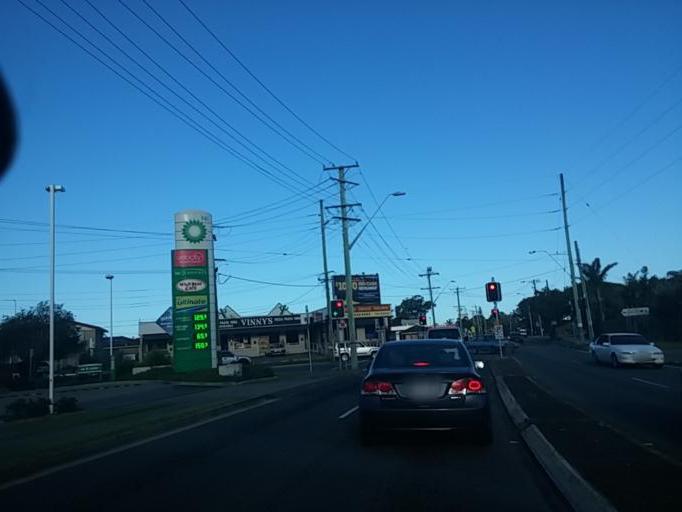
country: AU
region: New South Wales
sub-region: Tweed
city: Tweed Heads West
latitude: -28.1861
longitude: 153.5259
